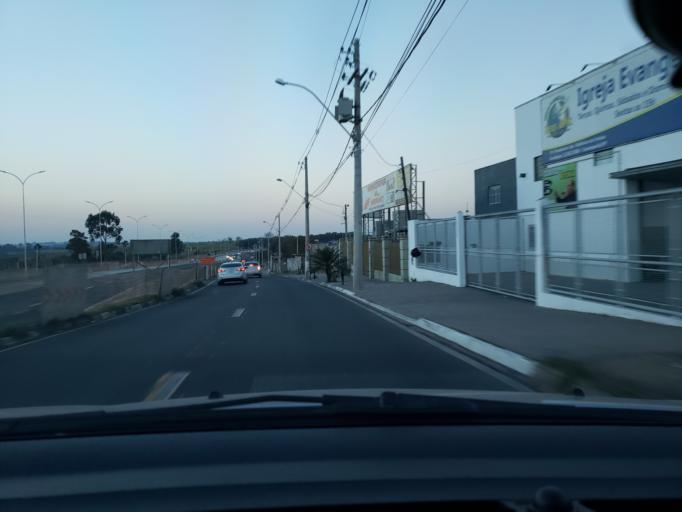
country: BR
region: Sao Paulo
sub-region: Campinas
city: Campinas
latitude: -22.9413
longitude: -47.1424
